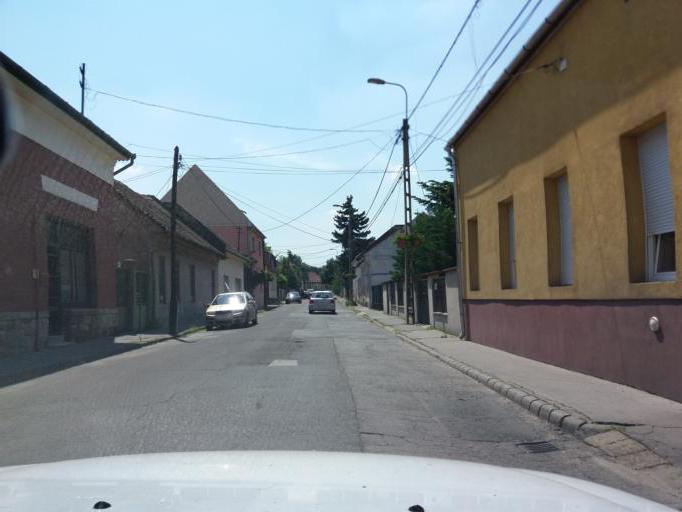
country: HU
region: Budapest
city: Budapest XI. keruelet
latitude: 47.4534
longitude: 19.0216
